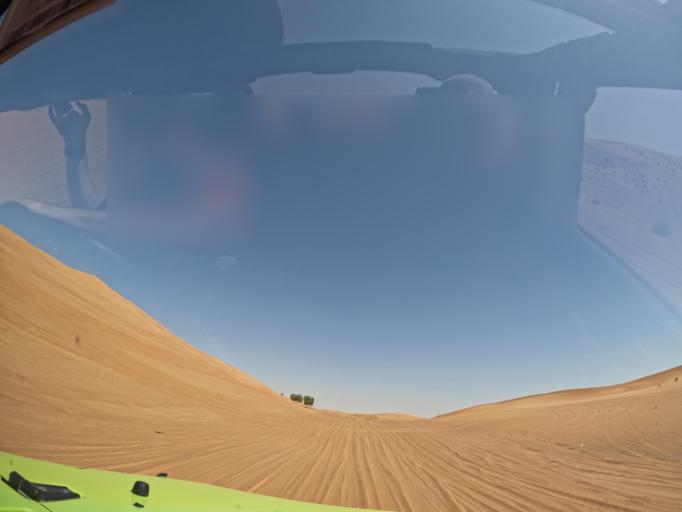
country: AE
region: Ash Shariqah
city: Adh Dhayd
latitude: 24.9721
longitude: 55.7208
